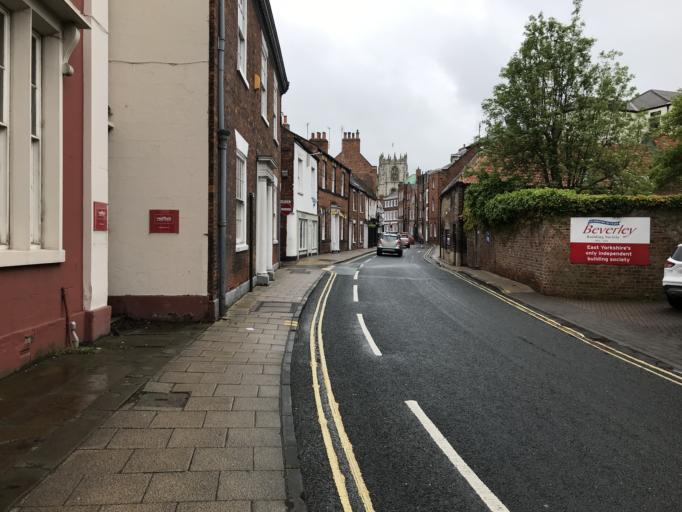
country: GB
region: England
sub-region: East Riding of Yorkshire
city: Beverley
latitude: 53.8424
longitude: -0.4330
